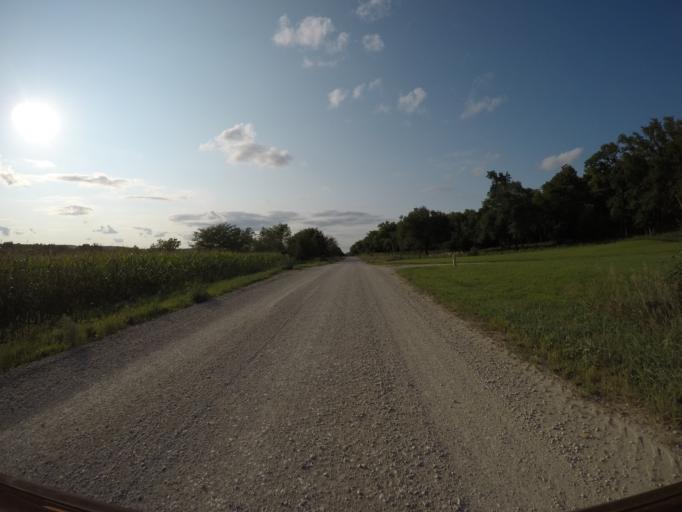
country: US
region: Kansas
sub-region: Wabaunsee County
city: Alma
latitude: 38.9310
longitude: -96.2307
